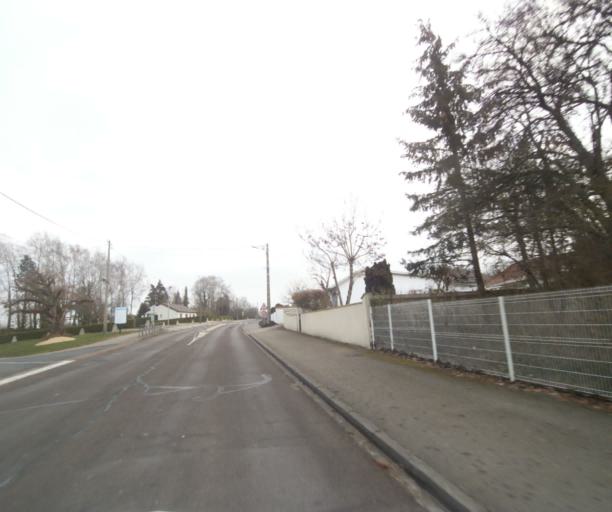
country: FR
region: Champagne-Ardenne
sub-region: Departement de la Haute-Marne
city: Chancenay
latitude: 48.6716
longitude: 4.9898
